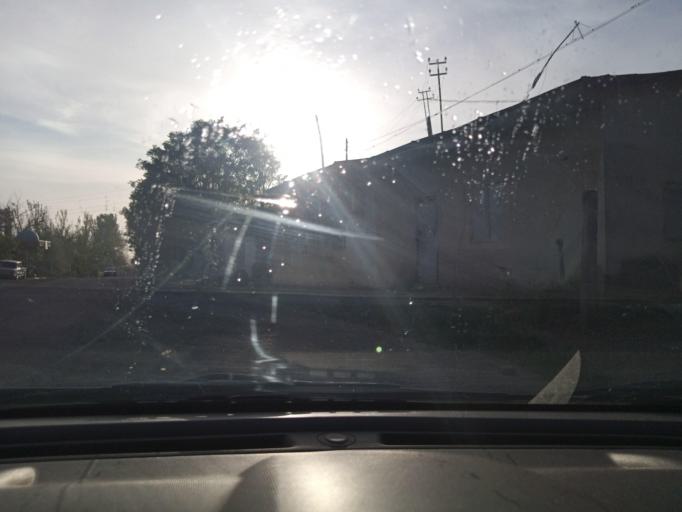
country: UZ
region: Toshkent
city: Parkent
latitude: 41.2475
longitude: 69.7631
